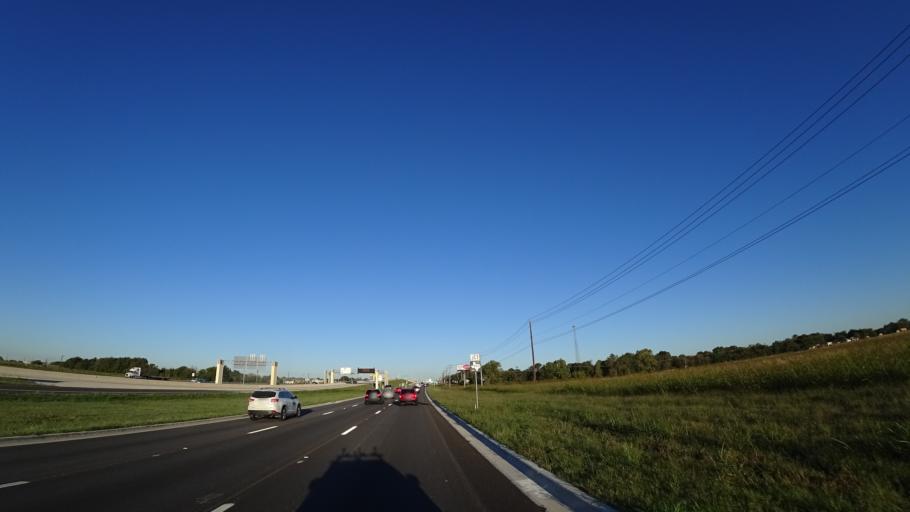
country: US
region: Texas
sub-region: Travis County
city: Hornsby Bend
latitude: 30.2009
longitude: -97.6345
